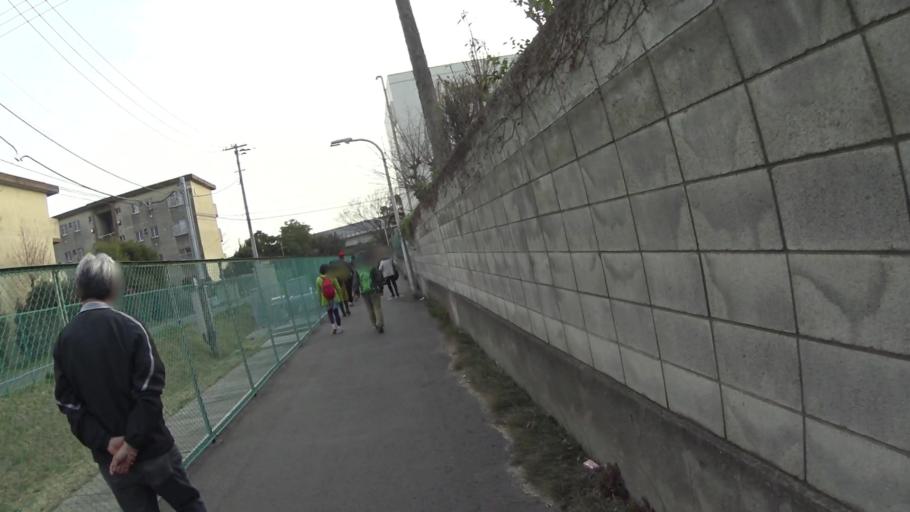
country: JP
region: Chiba
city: Funabashi
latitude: 35.6828
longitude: 140.0007
